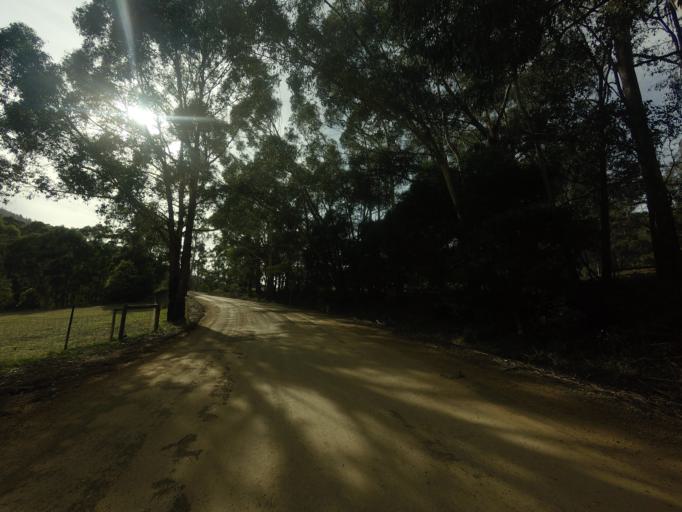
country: AU
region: Tasmania
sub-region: Huon Valley
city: Huonville
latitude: -43.0719
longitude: 147.0839
